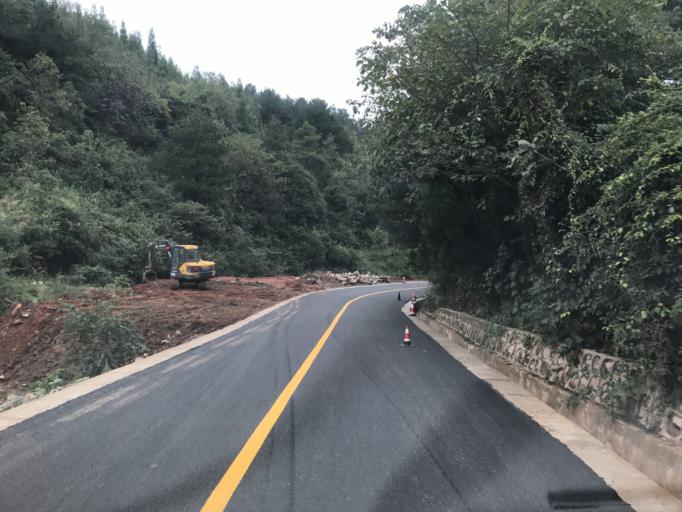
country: CN
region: Guizhou Sheng
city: Supu
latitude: 26.7367
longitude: 106.4371
